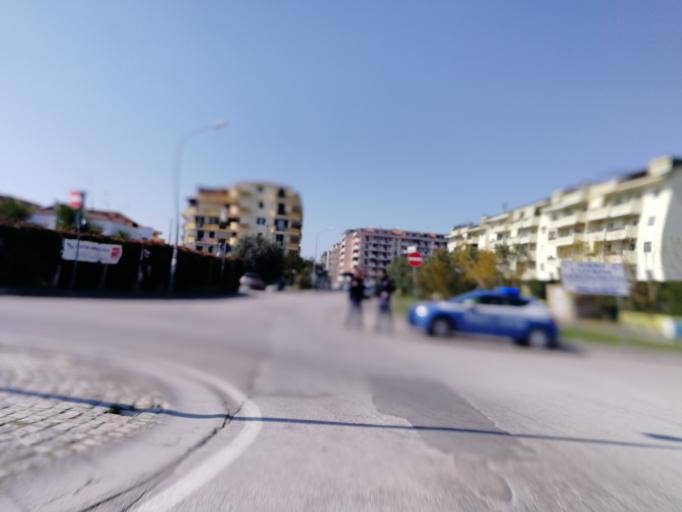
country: IT
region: Campania
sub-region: Provincia di Caserta
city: San Prisco
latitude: 41.0899
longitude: 14.2677
